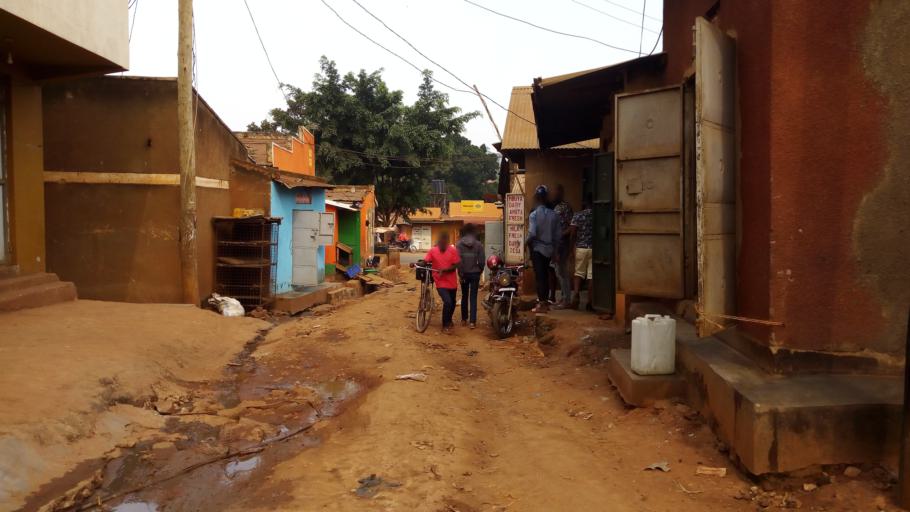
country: UG
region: Central Region
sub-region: Wakiso District
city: Kireka
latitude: 0.3215
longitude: 32.6351
